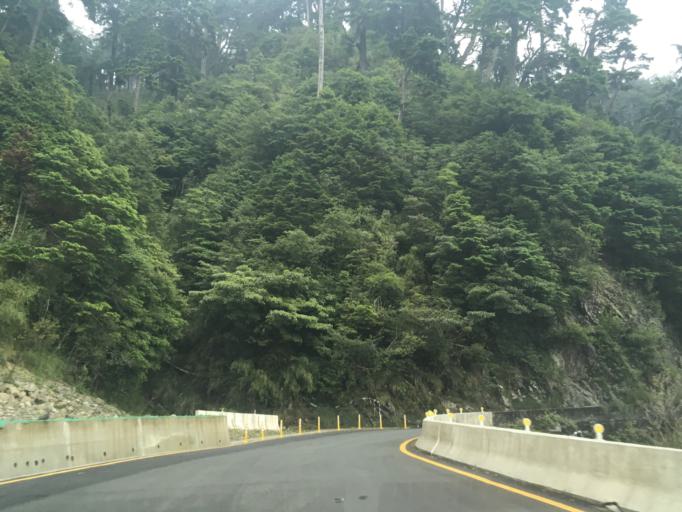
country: TW
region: Taiwan
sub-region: Nantou
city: Puli
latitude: 24.2713
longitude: 121.0266
